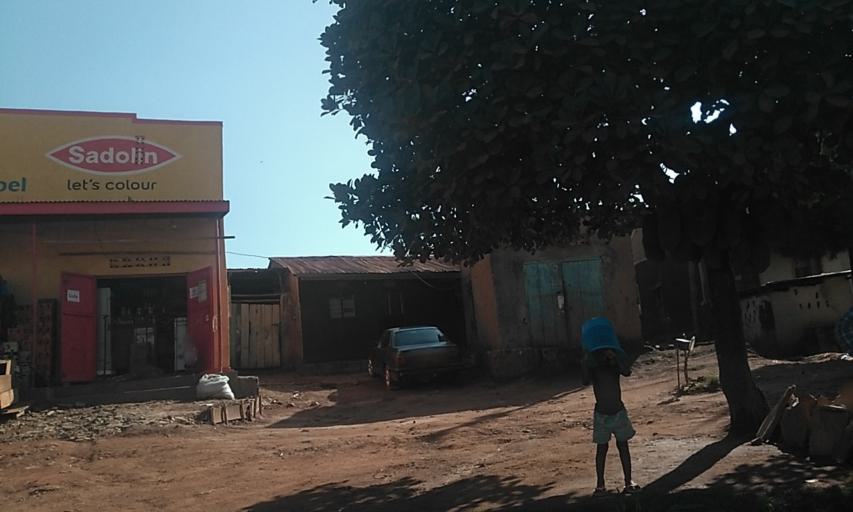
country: UG
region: Central Region
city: Kampala Central Division
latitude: 0.3254
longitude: 32.5388
